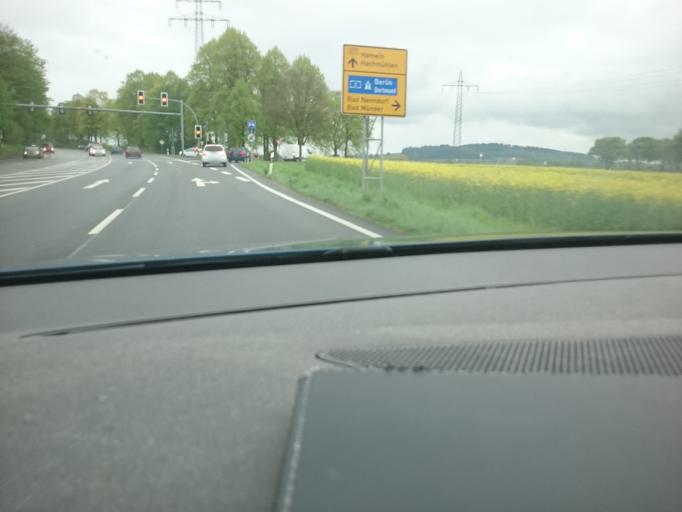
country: DE
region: Lower Saxony
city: Springe
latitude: 52.1973
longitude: 9.5290
